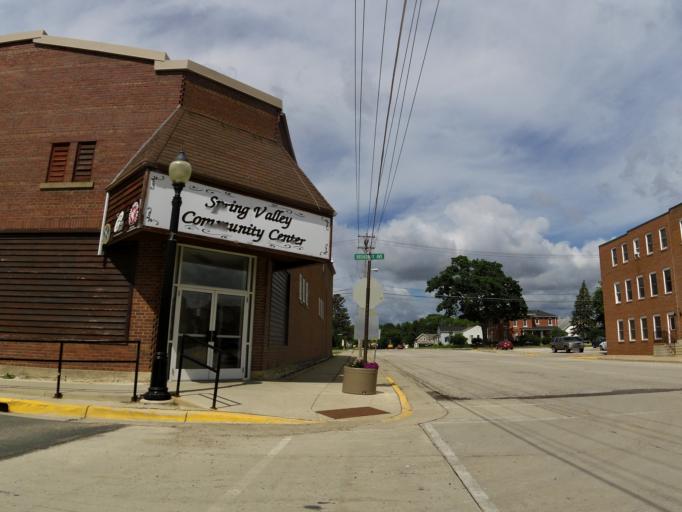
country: US
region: Minnesota
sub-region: Fillmore County
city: Spring Valley
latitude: 43.6869
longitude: -92.3910
